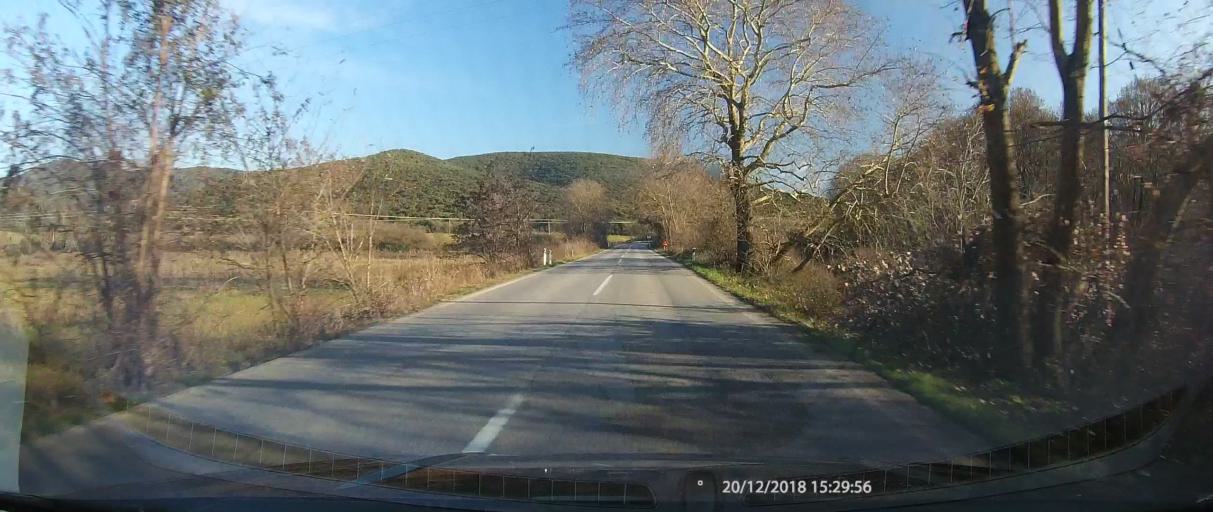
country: GR
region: Central Greece
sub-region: Nomos Fthiotidos
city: Lianokladhion
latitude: 38.9416
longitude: 22.2184
